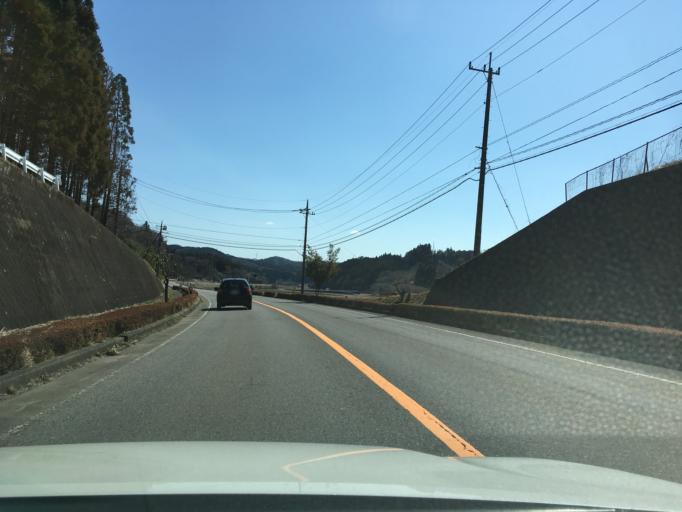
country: JP
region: Tochigi
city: Kuroiso
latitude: 37.0311
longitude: 140.1735
